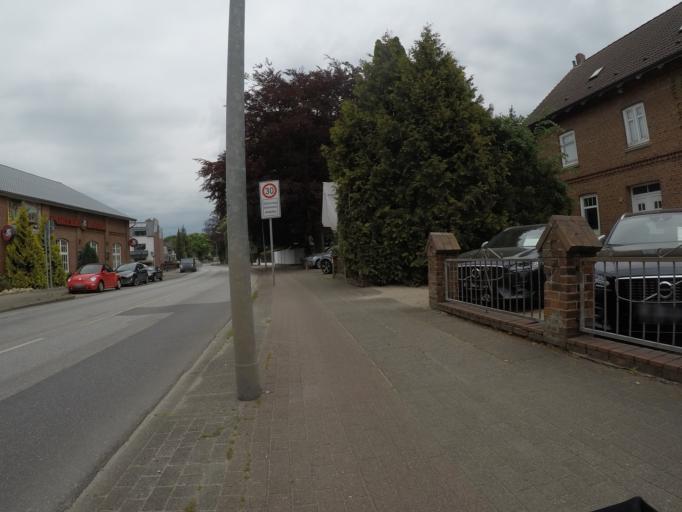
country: DE
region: Schleswig-Holstein
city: Norderstedt
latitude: 53.6753
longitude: 9.9684
